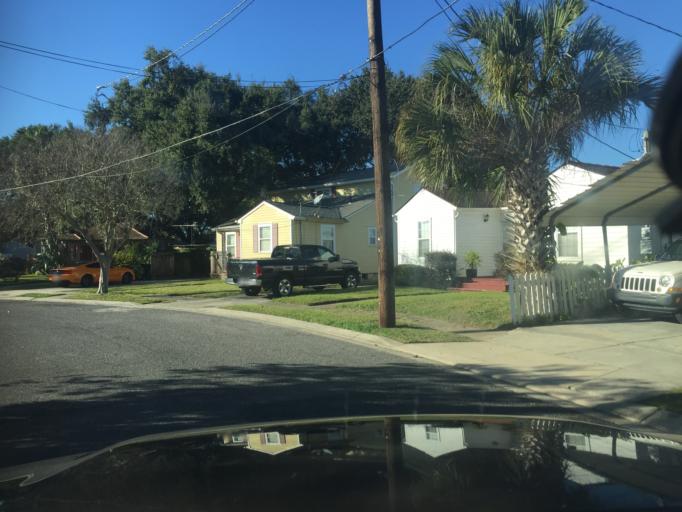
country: US
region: Louisiana
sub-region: Orleans Parish
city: New Orleans
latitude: 29.9898
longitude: -90.0780
